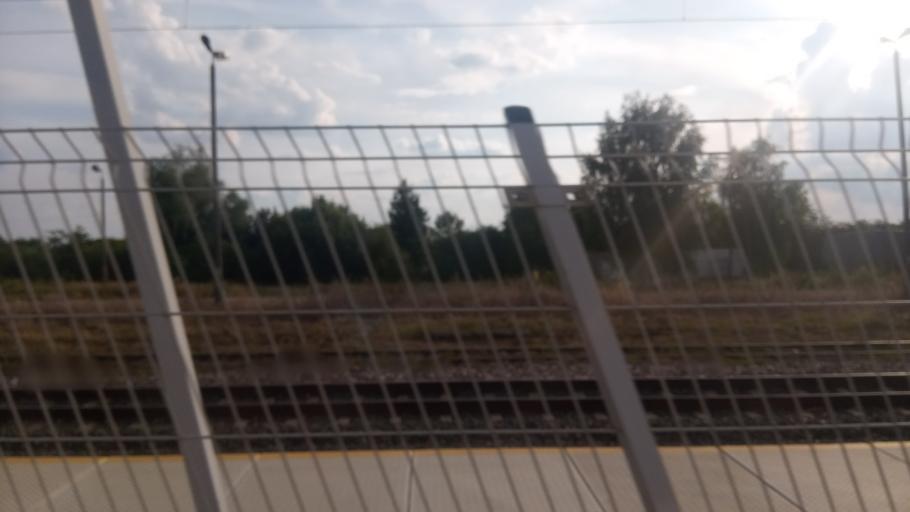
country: PL
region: Kujawsko-Pomorskie
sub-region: Powiat aleksandrowski
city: Waganiec
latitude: 52.8035
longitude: 18.8696
